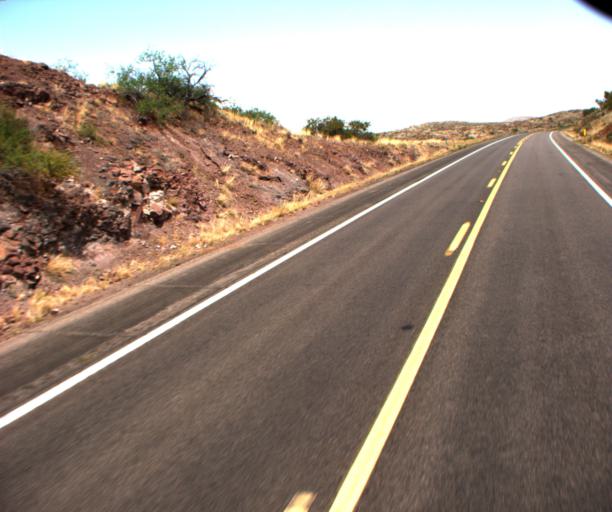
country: US
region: Arizona
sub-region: Greenlee County
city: Clifton
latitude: 32.7698
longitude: -109.2621
